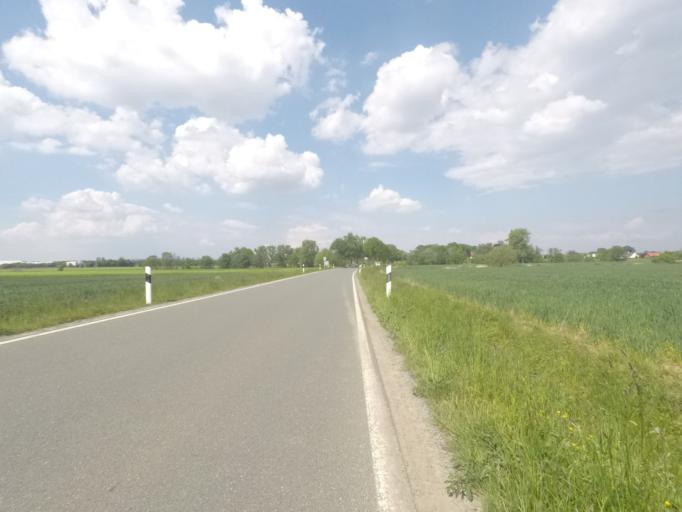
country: DE
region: North Rhine-Westphalia
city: Spenge
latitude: 52.1860
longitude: 8.5126
